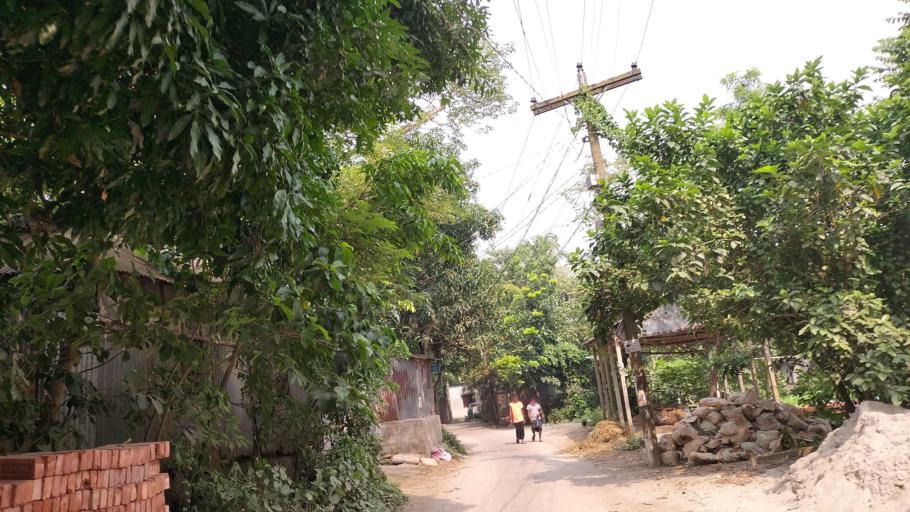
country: BD
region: Dhaka
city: Azimpur
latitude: 23.6894
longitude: 90.3027
